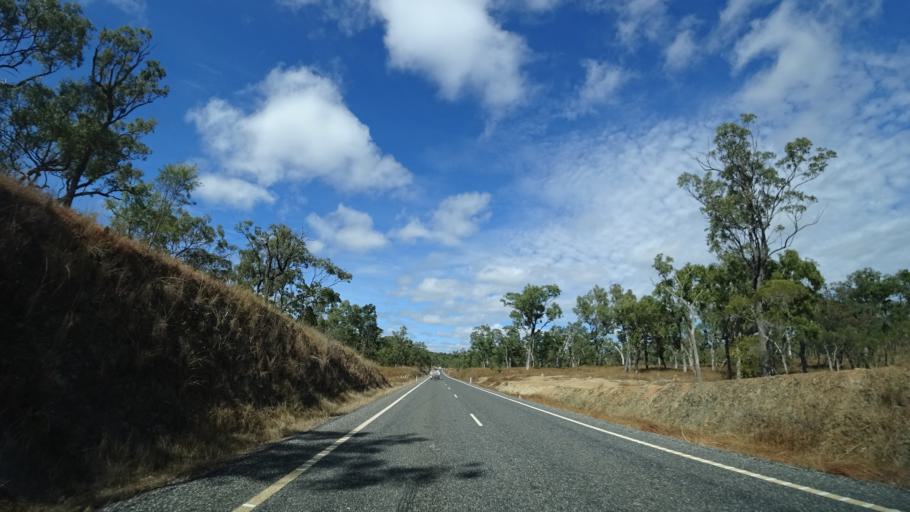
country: AU
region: Queensland
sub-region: Cairns
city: Port Douglas
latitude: -16.2835
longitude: 144.7150
